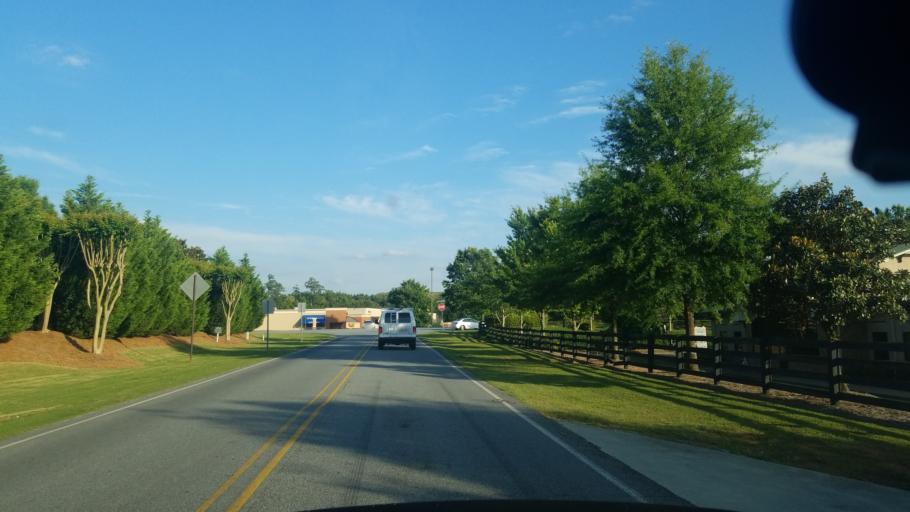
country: US
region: Georgia
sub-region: Fulton County
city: Johns Creek
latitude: 34.0860
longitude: -84.1607
